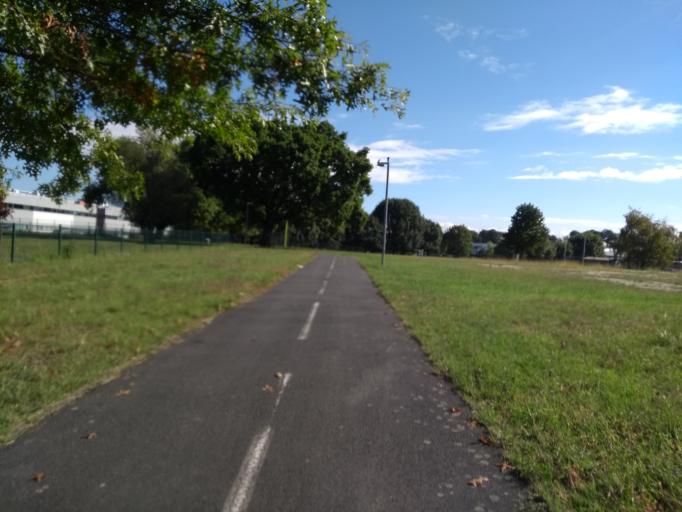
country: FR
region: Aquitaine
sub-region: Departement de la Gironde
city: Pessac
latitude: 44.7937
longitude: -0.6264
